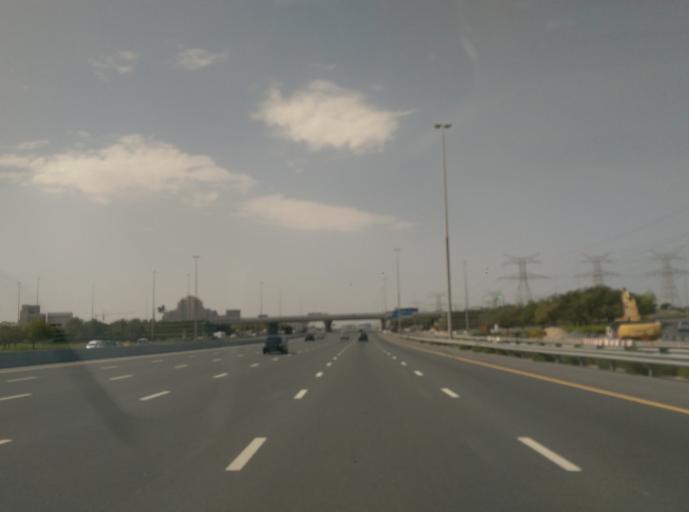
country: AE
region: Dubai
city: Dubai
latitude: 25.0793
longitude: 55.2125
